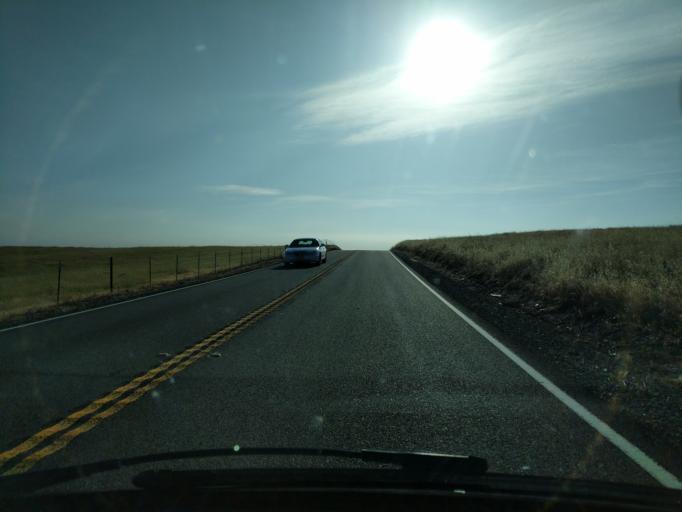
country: US
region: California
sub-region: Stanislaus County
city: East Oakdale
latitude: 37.9373
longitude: -120.7859
